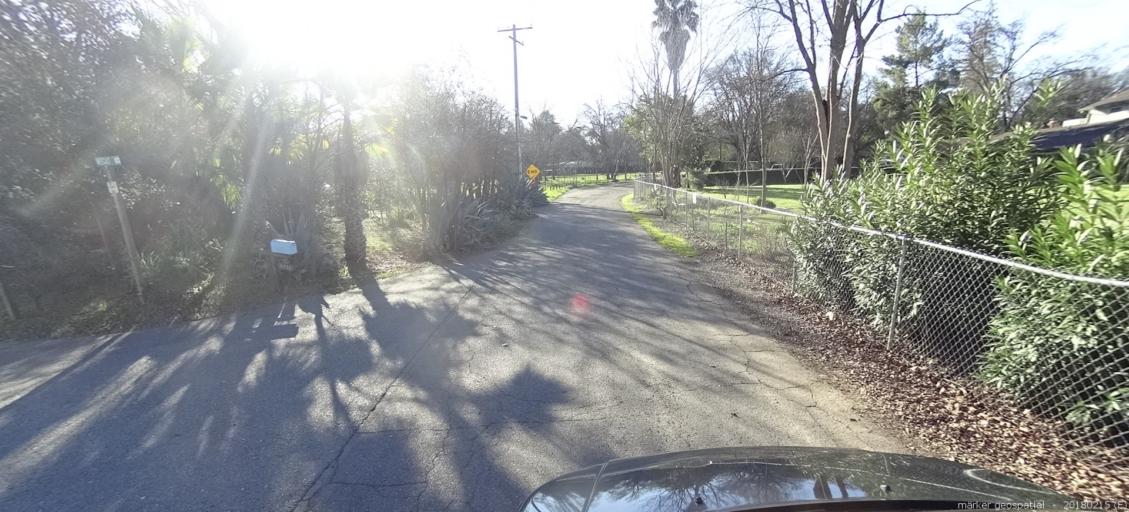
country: US
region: California
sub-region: Sacramento County
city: Foothill Farms
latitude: 38.6764
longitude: -121.3318
